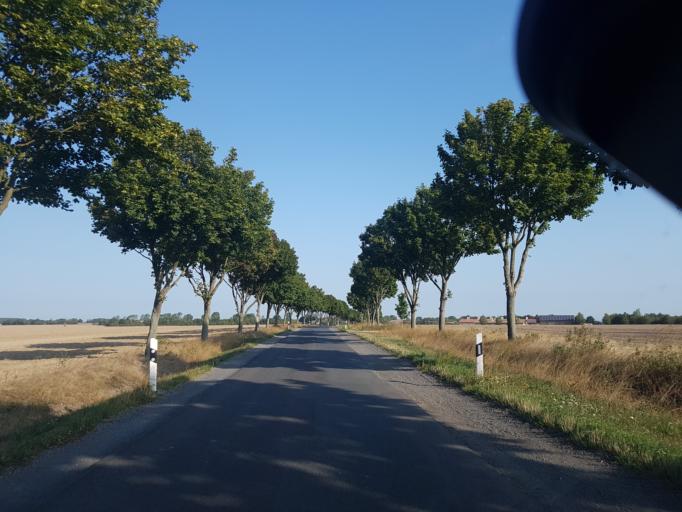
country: DE
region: Brandenburg
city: Niemegk
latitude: 52.0176
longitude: 12.6866
